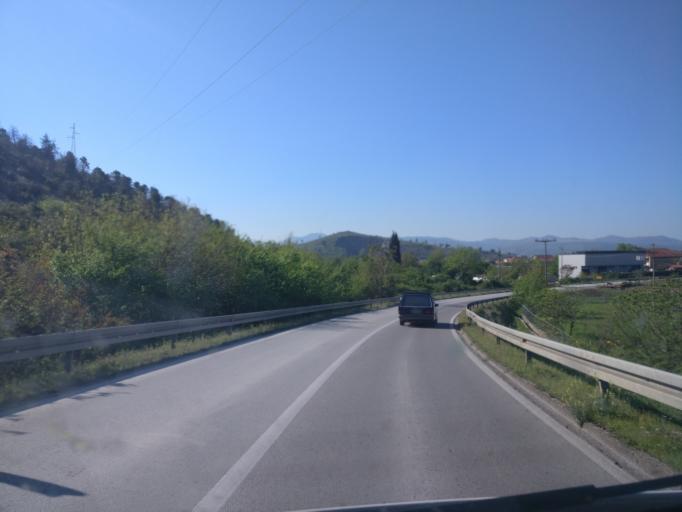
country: BA
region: Federation of Bosnia and Herzegovina
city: Tasovcici
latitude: 43.1108
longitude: 17.7223
